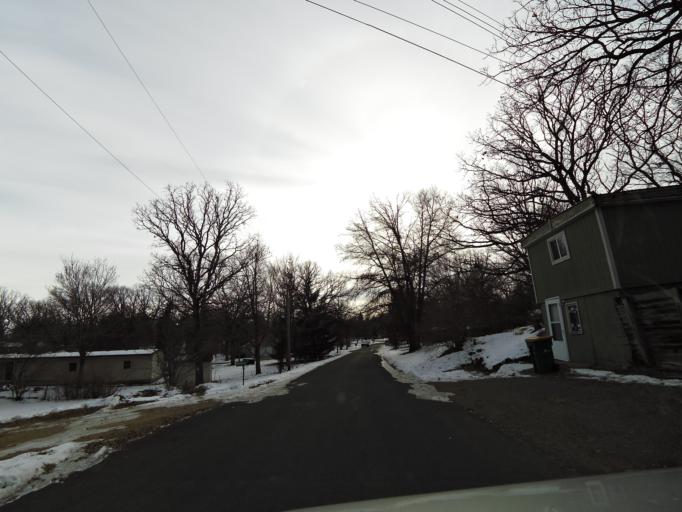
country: US
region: Minnesota
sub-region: Washington County
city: Lake Saint Croix Beach
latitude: 44.9180
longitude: -92.7732
